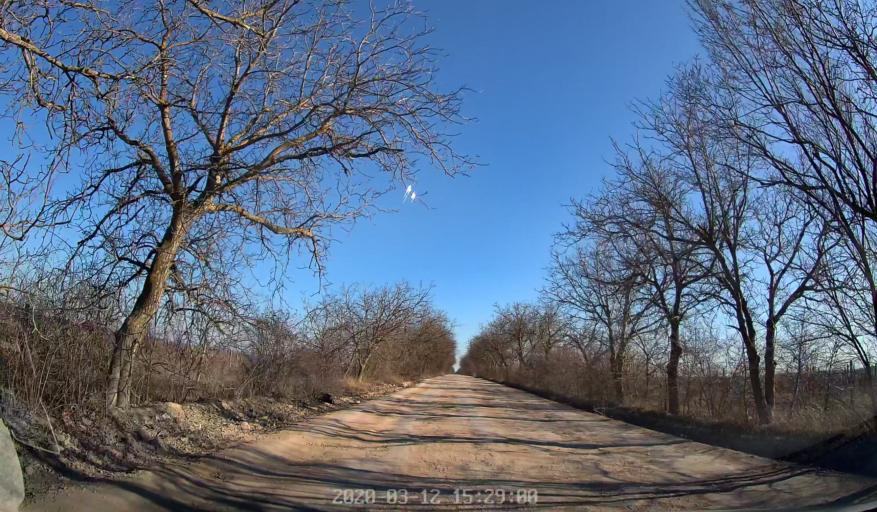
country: MD
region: Chisinau
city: Ciorescu
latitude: 47.1658
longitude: 28.9338
